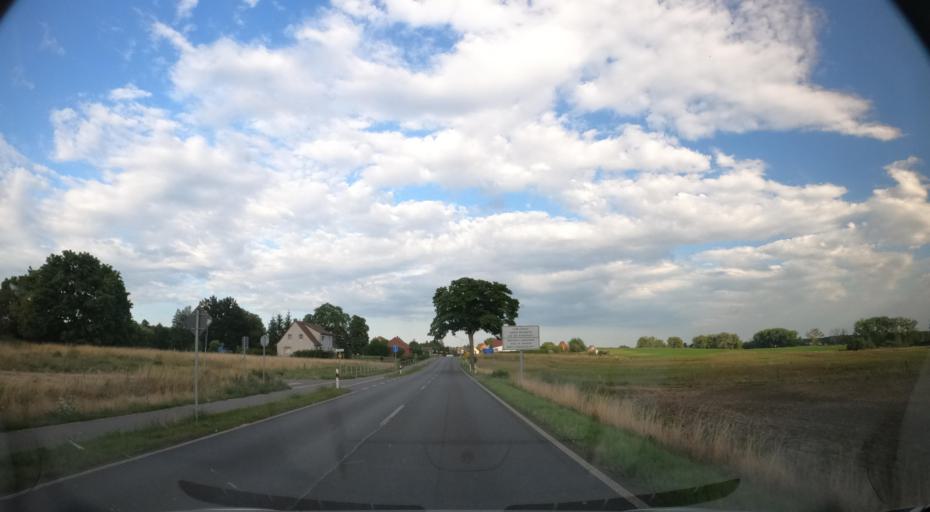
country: PL
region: West Pomeranian Voivodeship
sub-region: Powiat policki
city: Dobra
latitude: 53.4573
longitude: 14.3094
